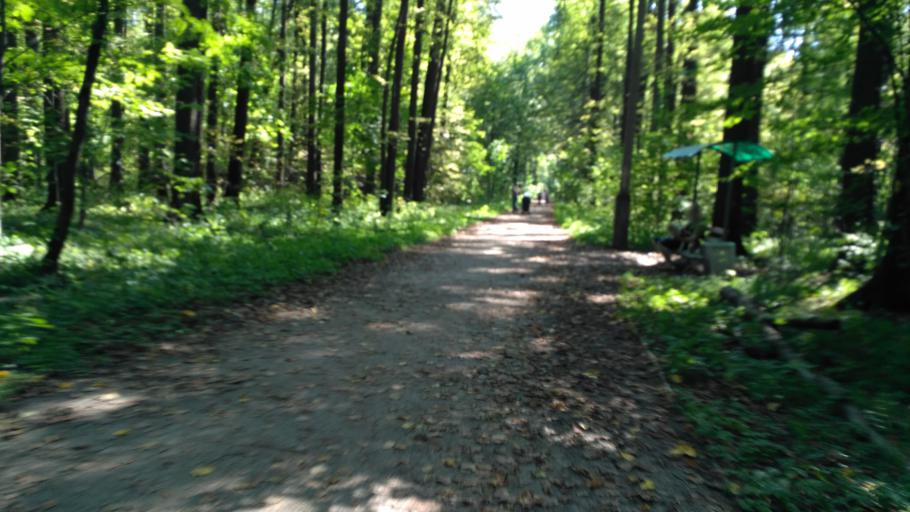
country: RU
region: Moscow
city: Ryazanskiy
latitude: 55.7707
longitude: 37.7593
